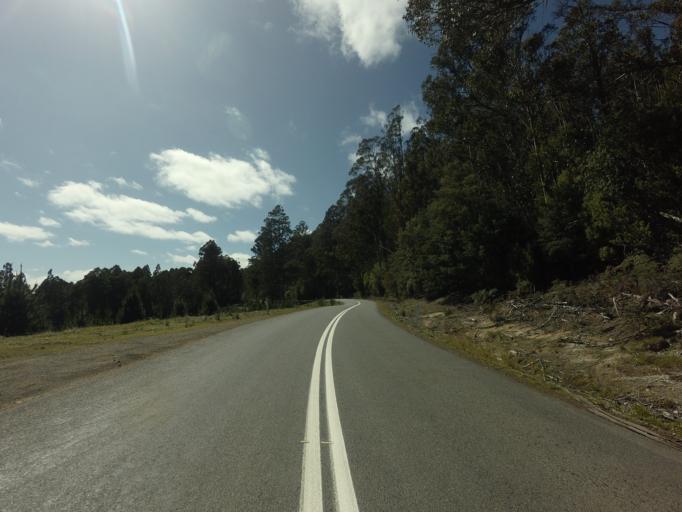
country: AU
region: Tasmania
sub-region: Derwent Valley
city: New Norfolk
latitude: -42.7407
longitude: 146.6592
